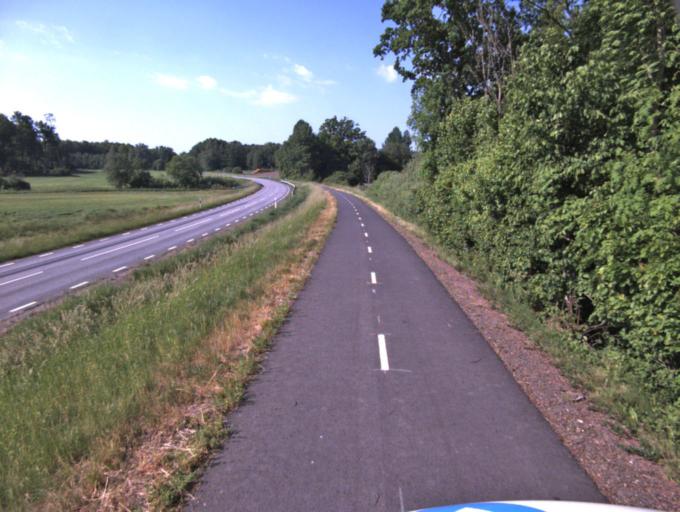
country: SE
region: Skane
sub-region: Kristianstads Kommun
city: Tollarp
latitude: 56.1530
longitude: 14.2639
